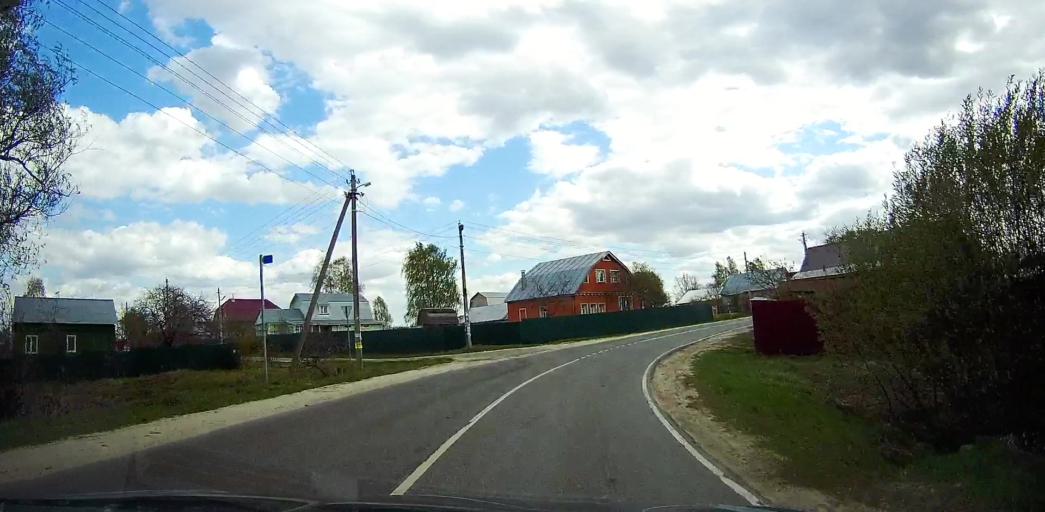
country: RU
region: Moskovskaya
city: Davydovo
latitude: 55.6455
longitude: 38.7507
